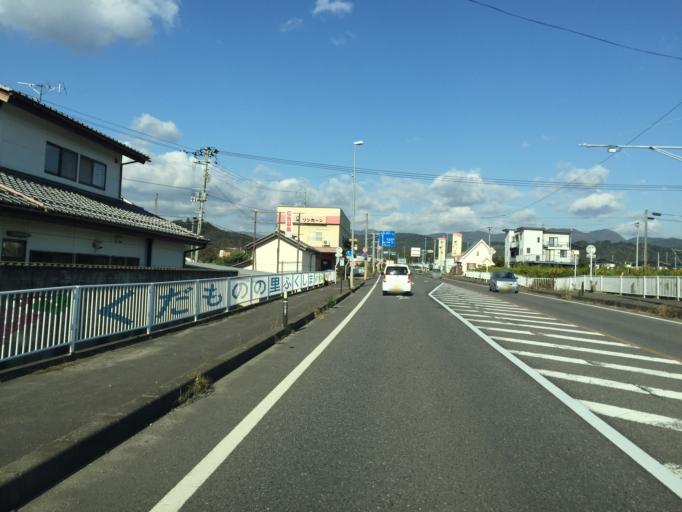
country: JP
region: Fukushima
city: Fukushima-shi
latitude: 37.8145
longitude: 140.4406
